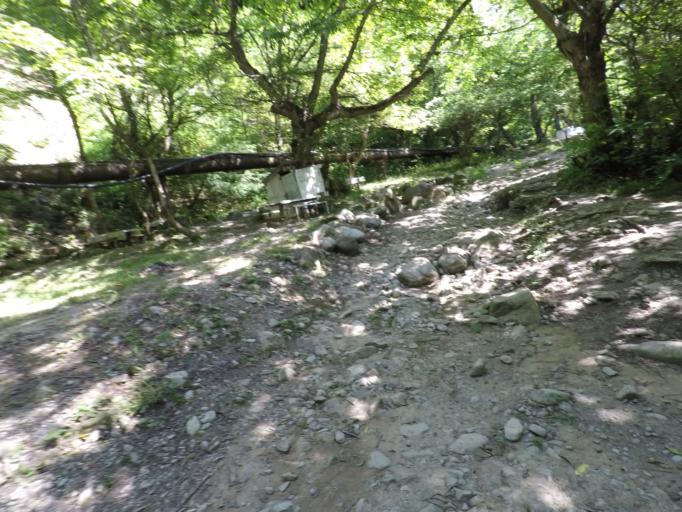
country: AZ
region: Qakh Rayon
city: Cinarli
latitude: 41.4893
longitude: 46.8563
